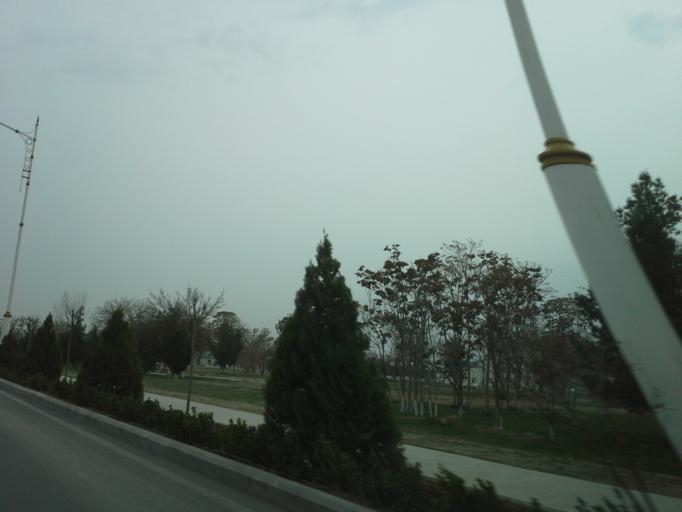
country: TM
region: Ahal
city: Ashgabat
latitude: 37.9642
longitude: 58.3599
